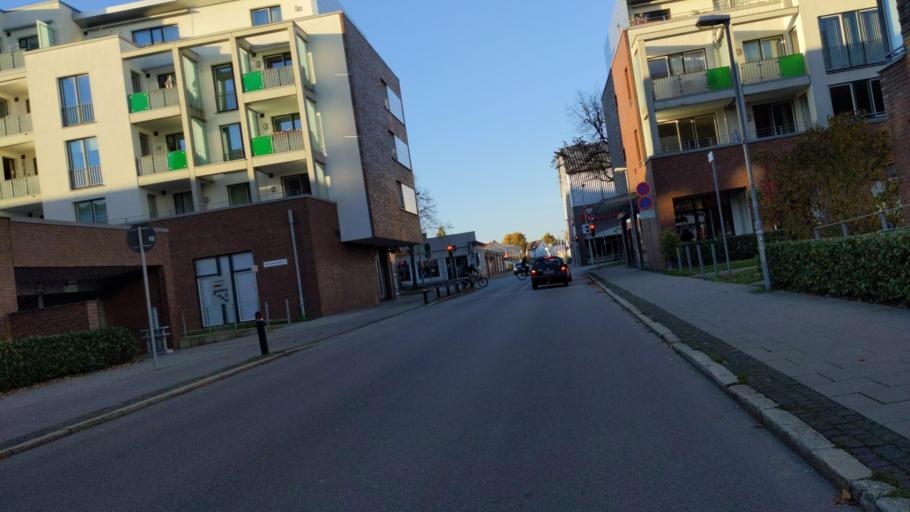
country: DE
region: Schleswig-Holstein
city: Luebeck
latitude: 53.8641
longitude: 10.7221
